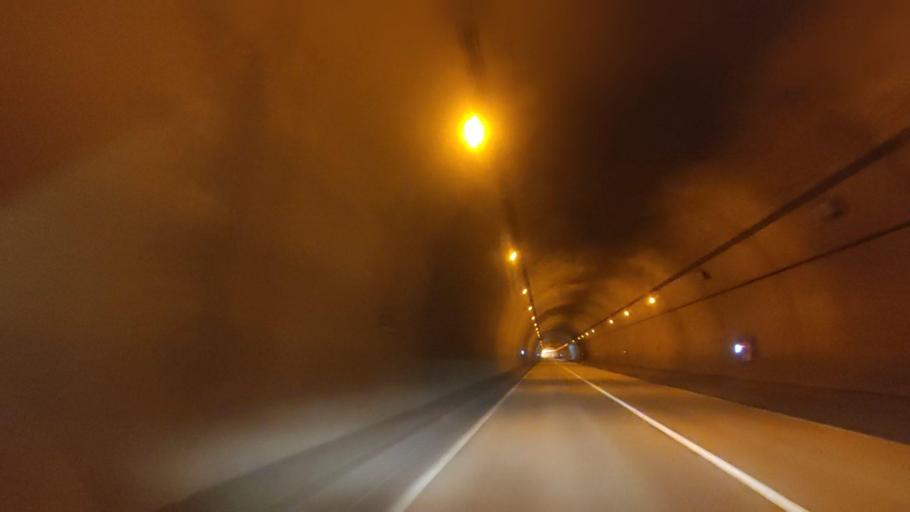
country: JP
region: Hokkaido
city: Date
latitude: 42.5576
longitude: 140.7639
